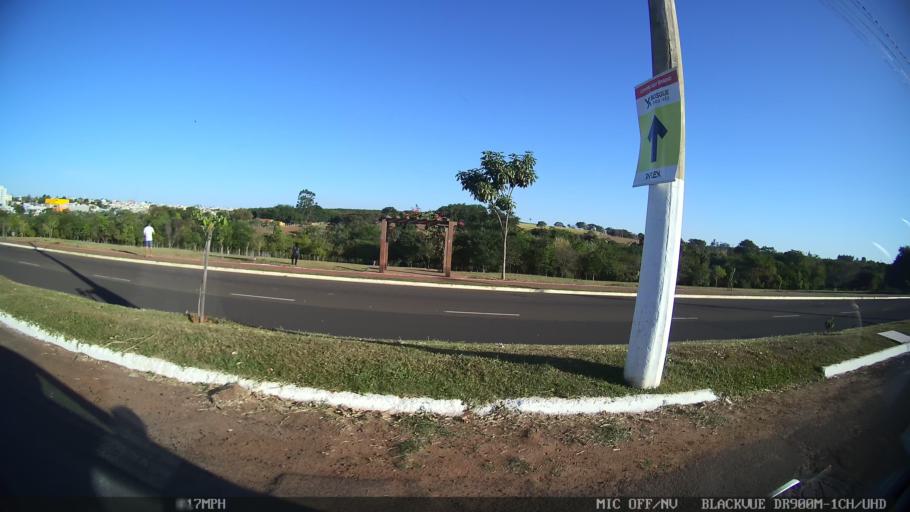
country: BR
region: Sao Paulo
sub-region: Guapiacu
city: Guapiacu
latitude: -20.7928
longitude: -49.2346
